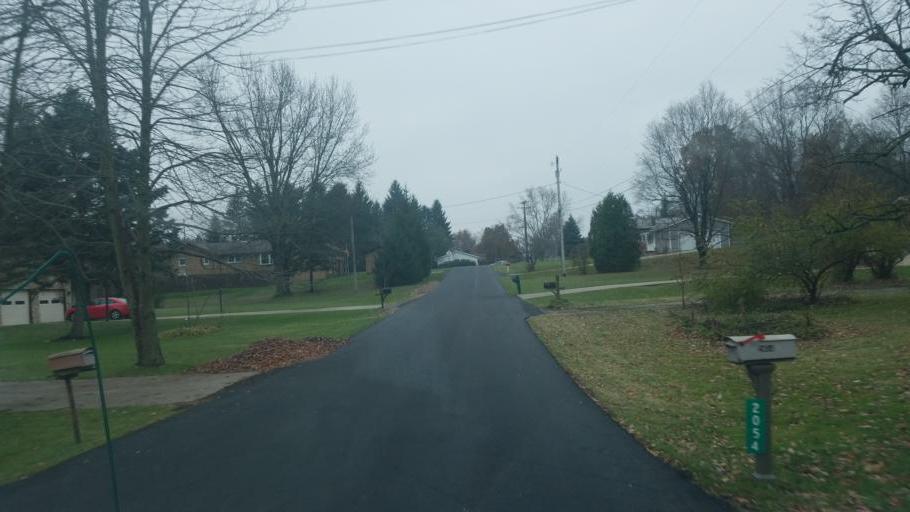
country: US
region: Ohio
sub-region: Richland County
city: Lexington
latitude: 40.7002
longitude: -82.5297
